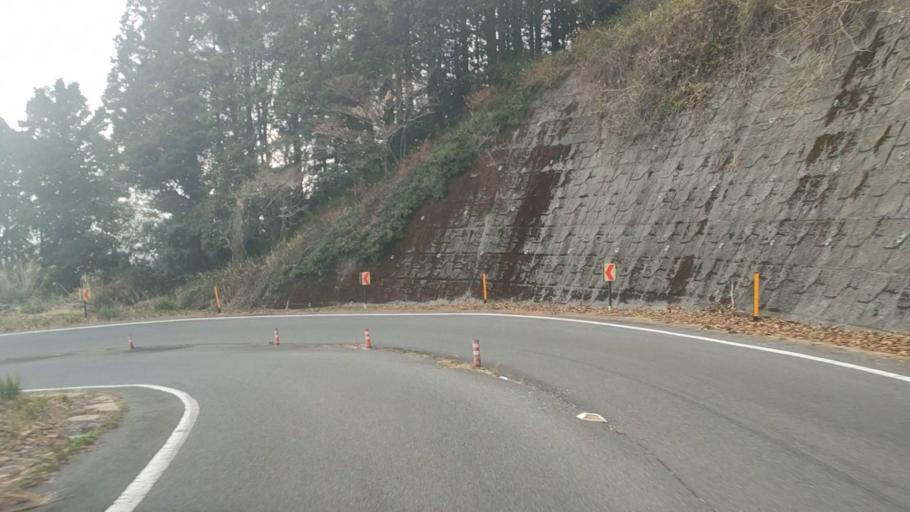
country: JP
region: Nagasaki
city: Shimabara
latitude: 32.7164
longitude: 130.2461
